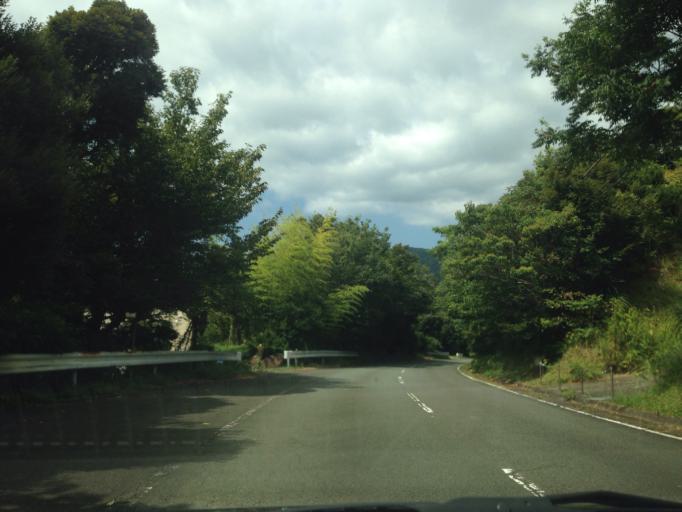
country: JP
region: Shizuoka
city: Shimoda
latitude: 34.6885
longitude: 138.7724
